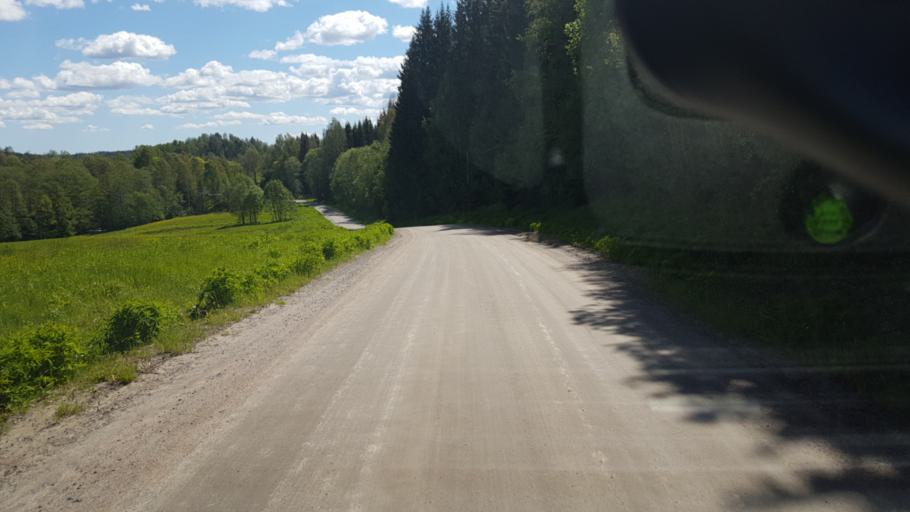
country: SE
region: Vaermland
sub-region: Sunne Kommun
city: Sunne
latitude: 59.6968
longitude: 12.8848
